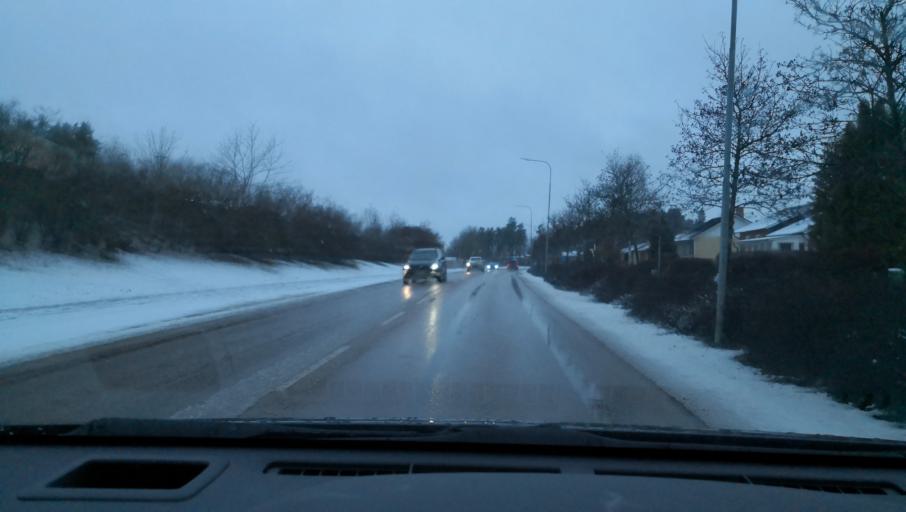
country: SE
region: Vaestmanland
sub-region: Kopings Kommun
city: Koping
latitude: 59.5207
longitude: 16.0048
